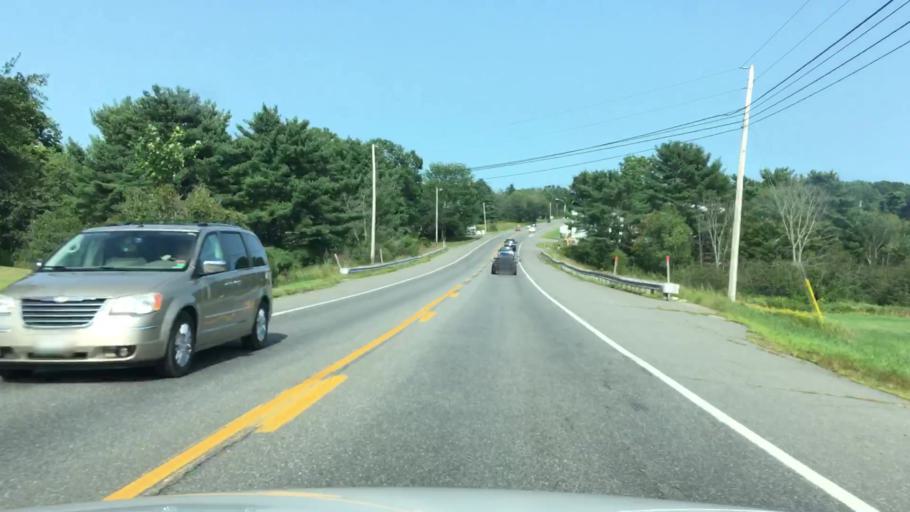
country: US
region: Maine
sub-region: Lincoln County
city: Nobleboro
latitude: 44.1015
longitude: -69.4486
